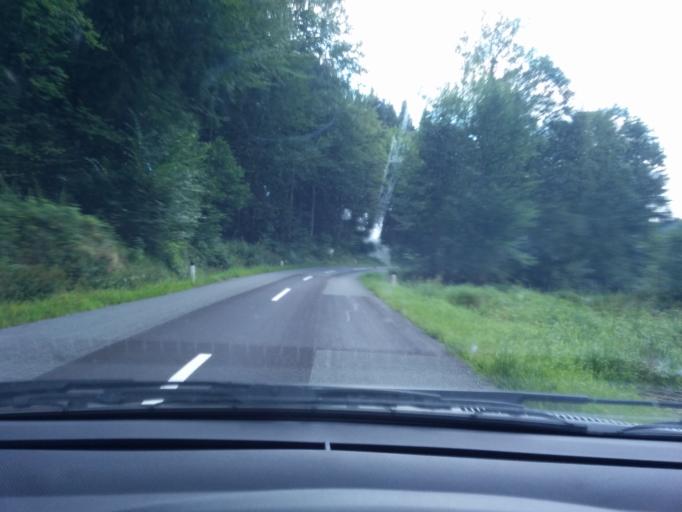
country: AT
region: Upper Austria
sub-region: Politischer Bezirk Rohrbach
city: Ulrichsberg
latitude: 48.7235
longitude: 13.8949
